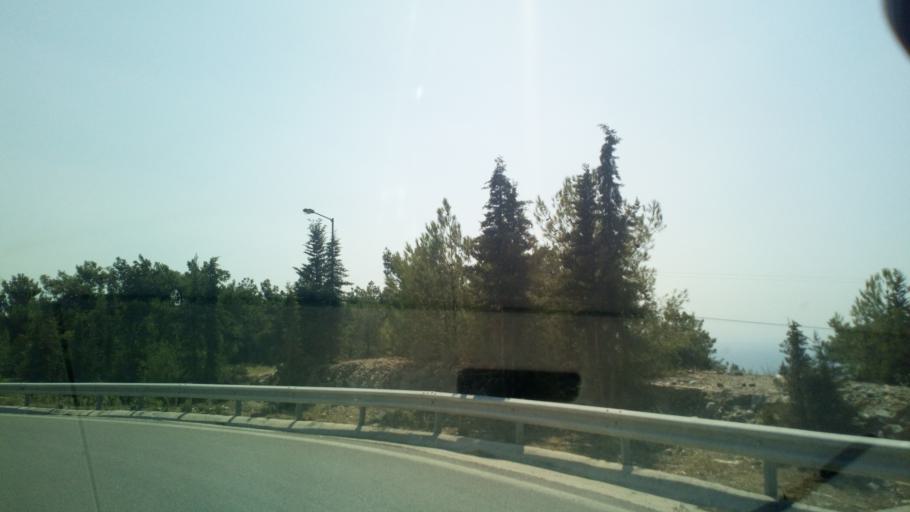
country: GR
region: Central Macedonia
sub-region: Nomos Thessalonikis
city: Agios Pavlos
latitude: 40.6435
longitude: 22.9690
